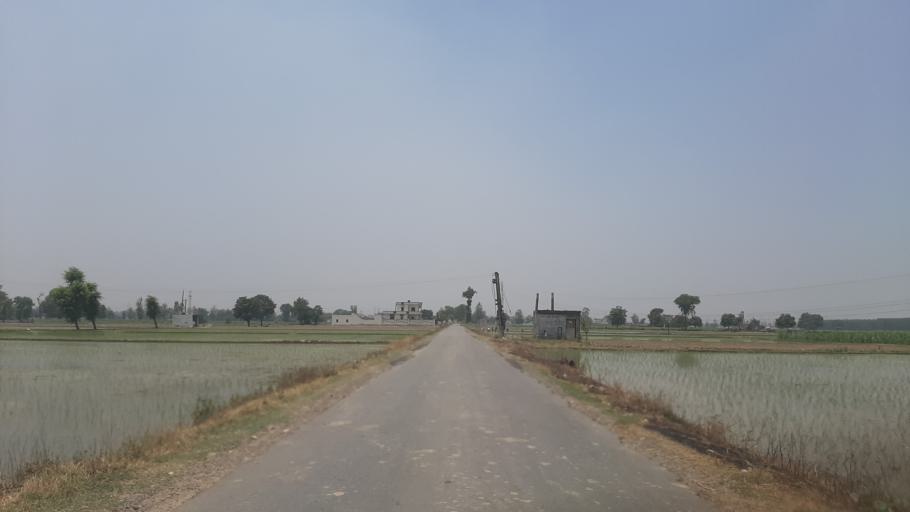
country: IN
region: Haryana
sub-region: Yamunanagar
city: Yamunanagar
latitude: 30.1651
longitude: 77.2397
